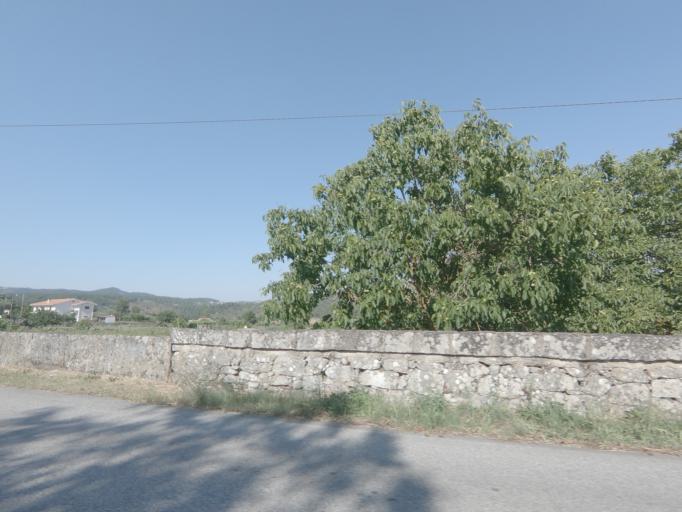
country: PT
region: Viseu
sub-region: Moimenta da Beira
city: Moimenta da Beira
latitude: 40.9709
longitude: -7.5910
